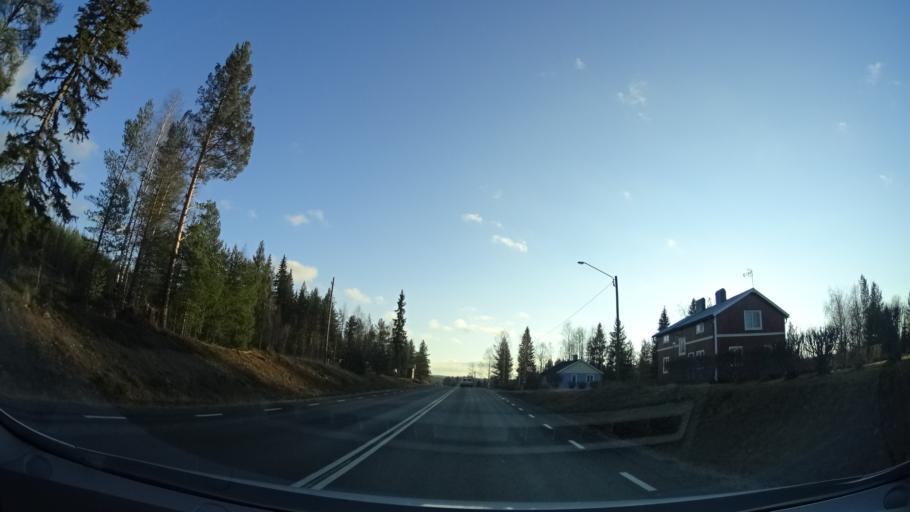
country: SE
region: Vaesterbotten
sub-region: Lycksele Kommun
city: Lycksele
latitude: 64.7452
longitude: 18.6682
